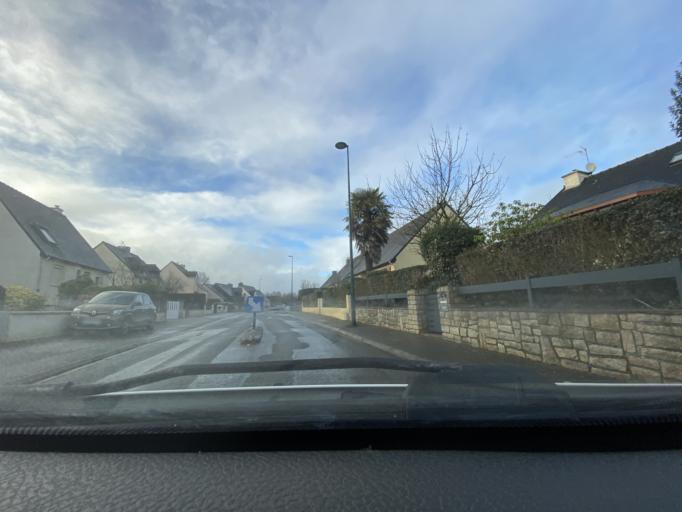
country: FR
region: Brittany
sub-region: Departement d'Ille-et-Vilaine
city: Melesse
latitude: 48.2235
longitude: -1.7023
